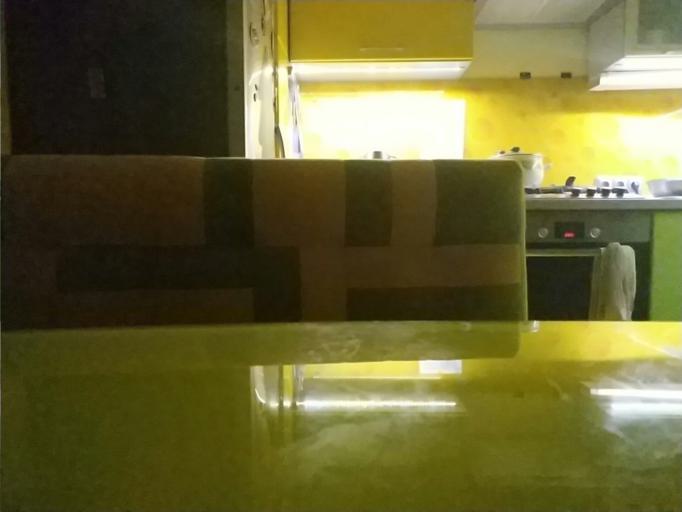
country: RU
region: Republic of Karelia
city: Pyaozerskiy
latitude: 65.8708
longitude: 30.4407
